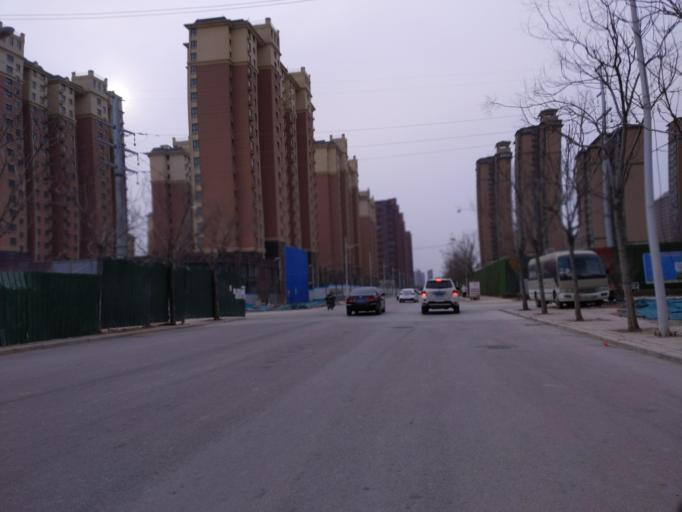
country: CN
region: Henan Sheng
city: Zhongyuanlu
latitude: 35.7426
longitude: 115.0746
